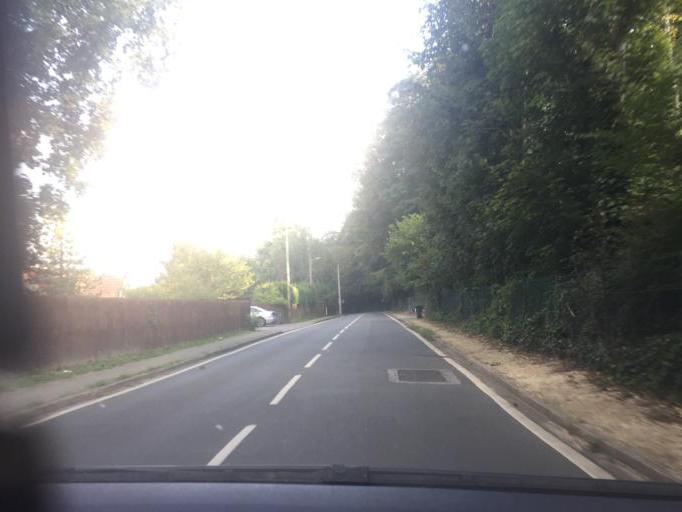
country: FR
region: Ile-de-France
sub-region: Departement des Yvelines
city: Les Loges-en-Josas
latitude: 48.7649
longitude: 2.1554
